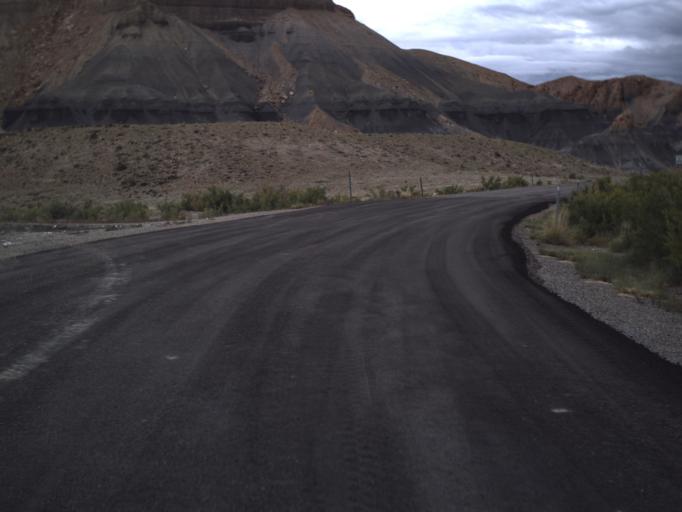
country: US
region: Utah
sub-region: Emery County
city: Ferron
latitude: 38.8151
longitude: -111.2114
